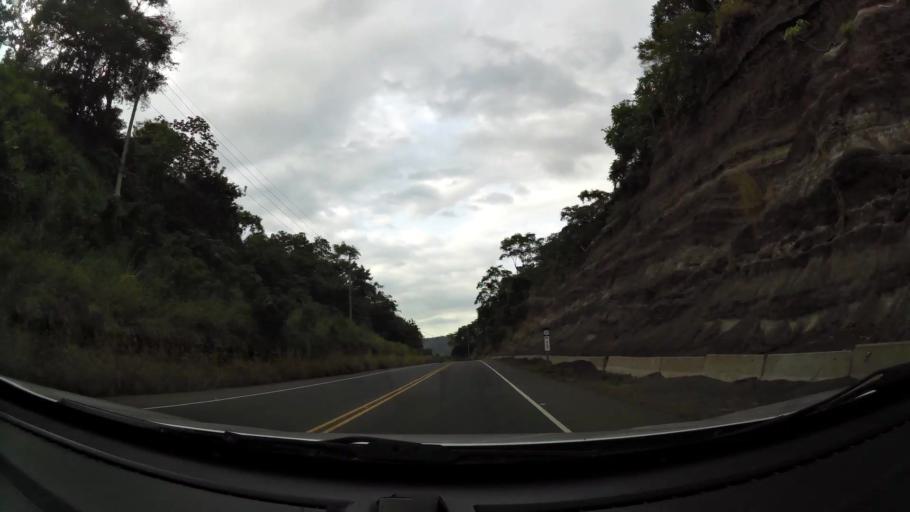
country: CR
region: Puntarenas
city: Esparza
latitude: 9.9176
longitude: -84.6841
